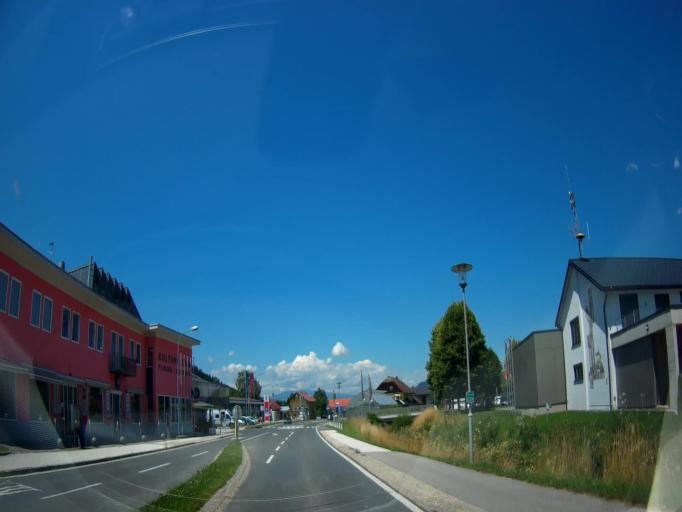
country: AT
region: Carinthia
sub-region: Politischer Bezirk Volkermarkt
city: Bleiburg/Pliberk
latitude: 46.5903
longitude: 14.7957
